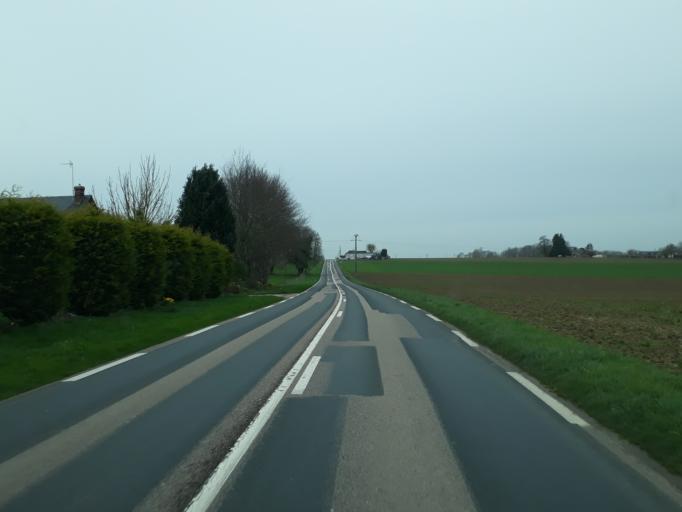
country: FR
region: Haute-Normandie
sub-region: Departement de la Seine-Maritime
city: Beuzeville-la-Grenier
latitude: 49.6082
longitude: 0.4129
